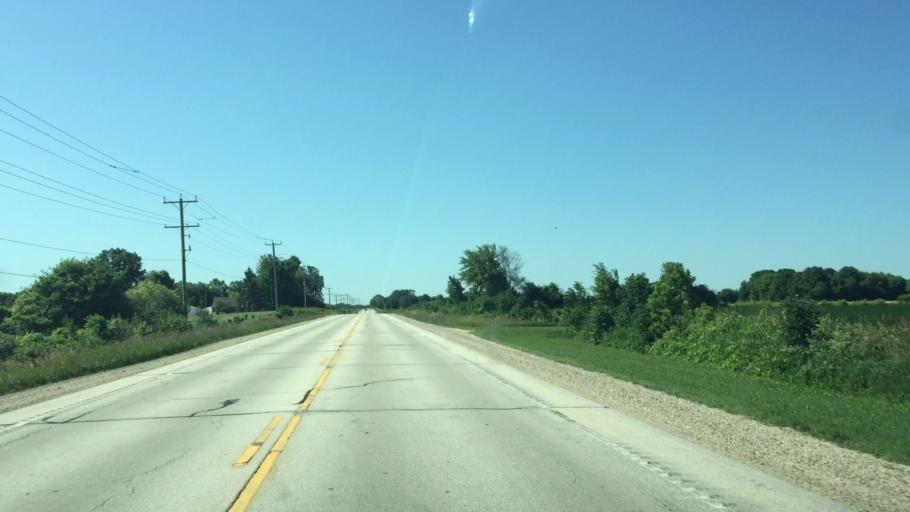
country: US
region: Wisconsin
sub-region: Calumet County
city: Sherwood
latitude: 44.1525
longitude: -88.2648
